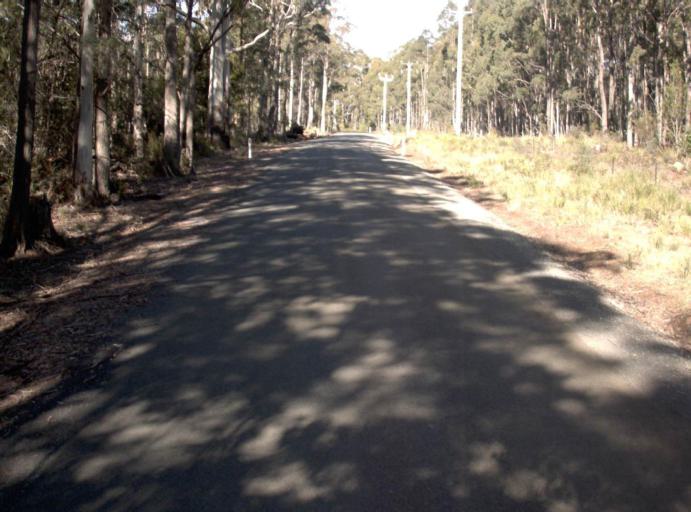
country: AU
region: Tasmania
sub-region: Launceston
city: Mayfield
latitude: -41.3169
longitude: 147.2075
